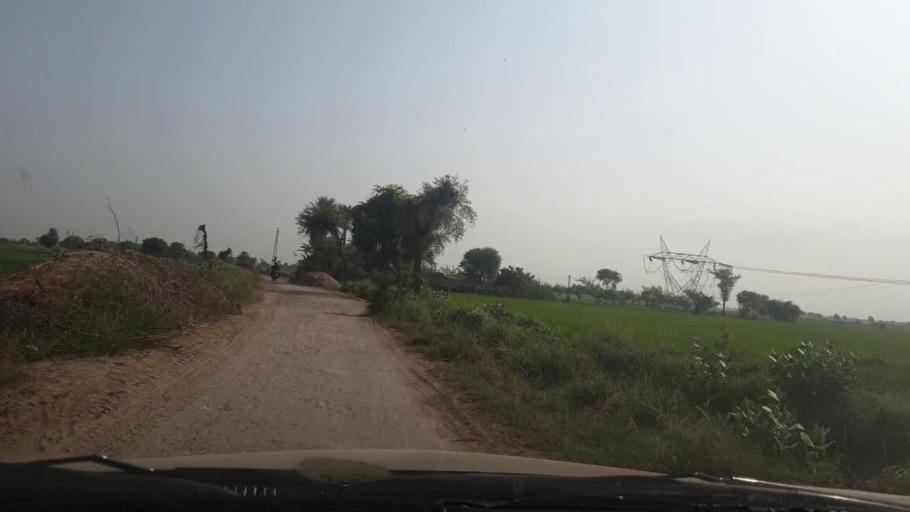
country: PK
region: Sindh
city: Larkana
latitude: 27.5831
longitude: 68.1860
